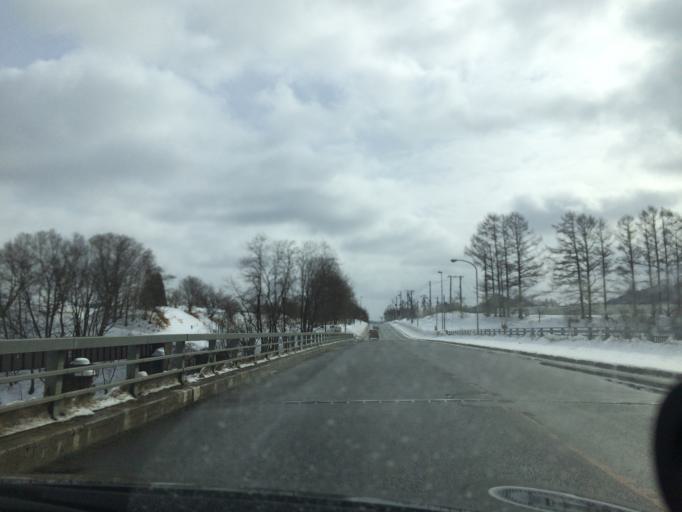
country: JP
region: Hokkaido
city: Iwamizawa
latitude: 42.9713
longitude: 142.0083
